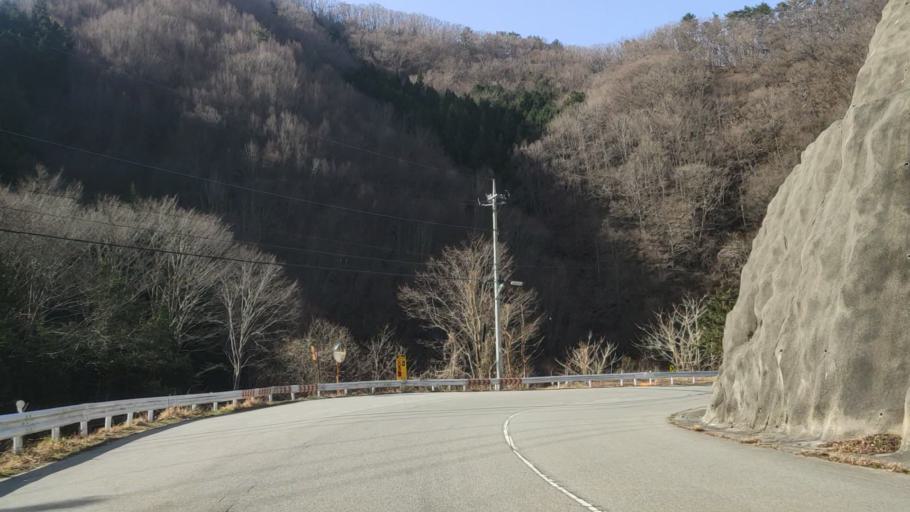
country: JP
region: Yamanashi
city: Fujikawaguchiko
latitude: 35.5496
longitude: 138.6596
